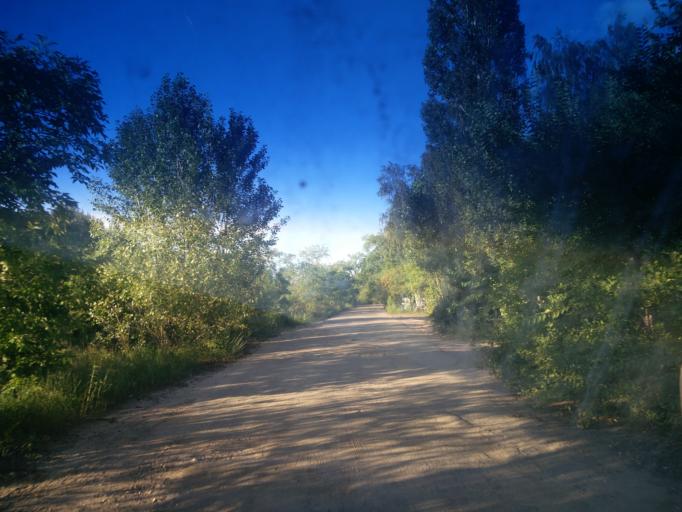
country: RU
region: Voronezj
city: Pridonskoy
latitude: 51.6710
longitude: 39.1062
